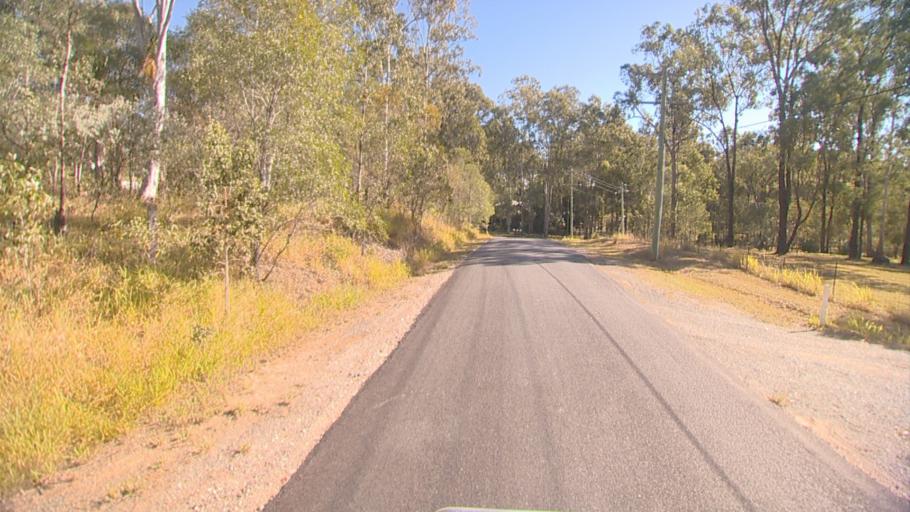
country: AU
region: Queensland
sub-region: Logan
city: Chambers Flat
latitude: -27.8093
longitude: 153.0829
